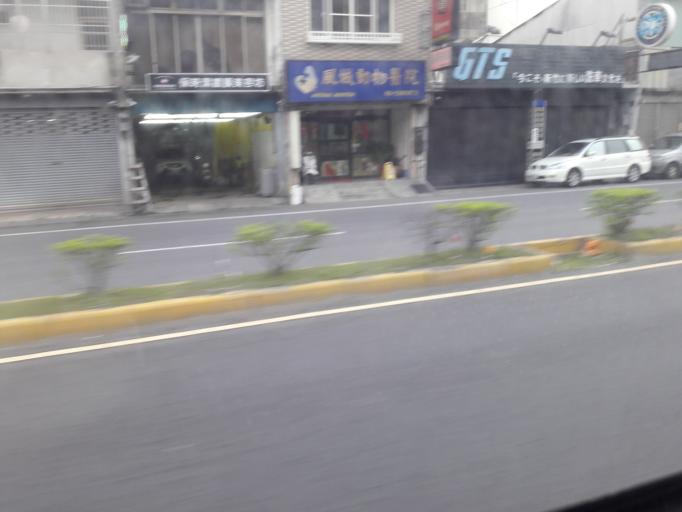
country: TW
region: Taiwan
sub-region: Hsinchu
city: Hsinchu
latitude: 24.7974
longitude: 120.9545
